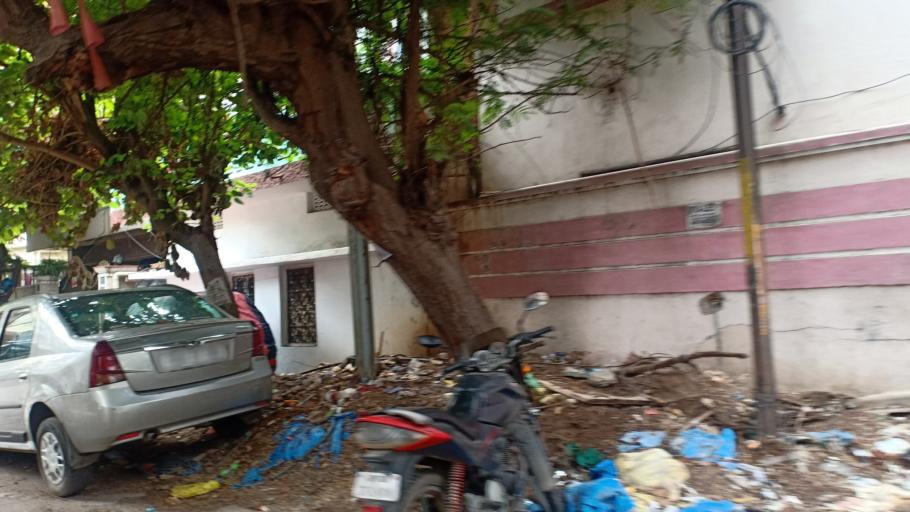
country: IN
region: Telangana
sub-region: Hyderabad
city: Hyderabad
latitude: 17.4347
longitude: 78.4404
